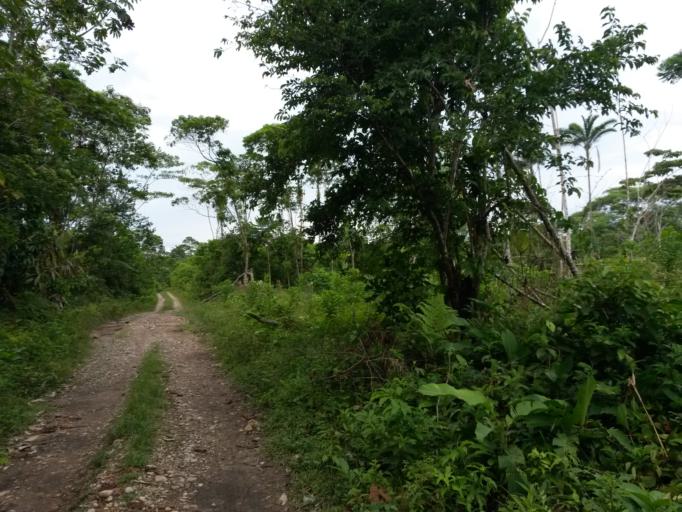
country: CO
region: Putumayo
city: Puerto Guzman
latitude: 1.0192
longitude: -76.3698
